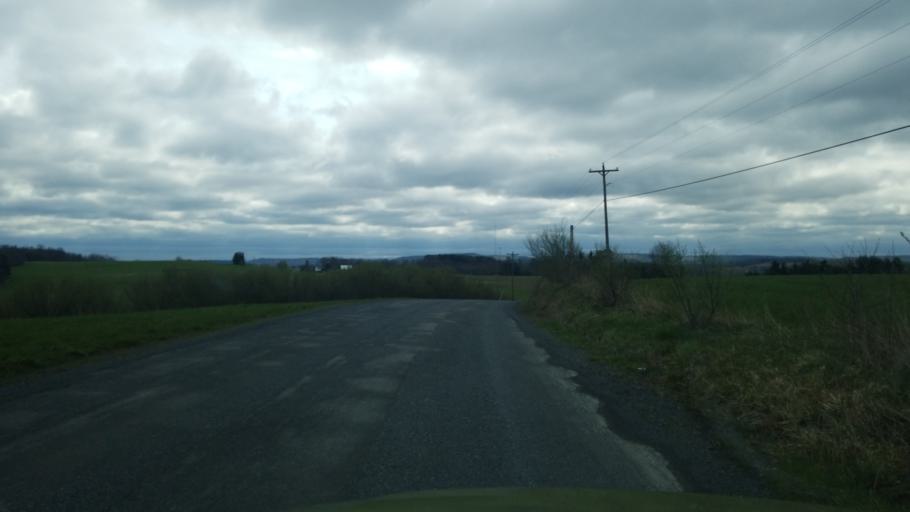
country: US
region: Pennsylvania
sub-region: Clearfield County
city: Clearfield
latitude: 41.0799
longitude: -78.3848
